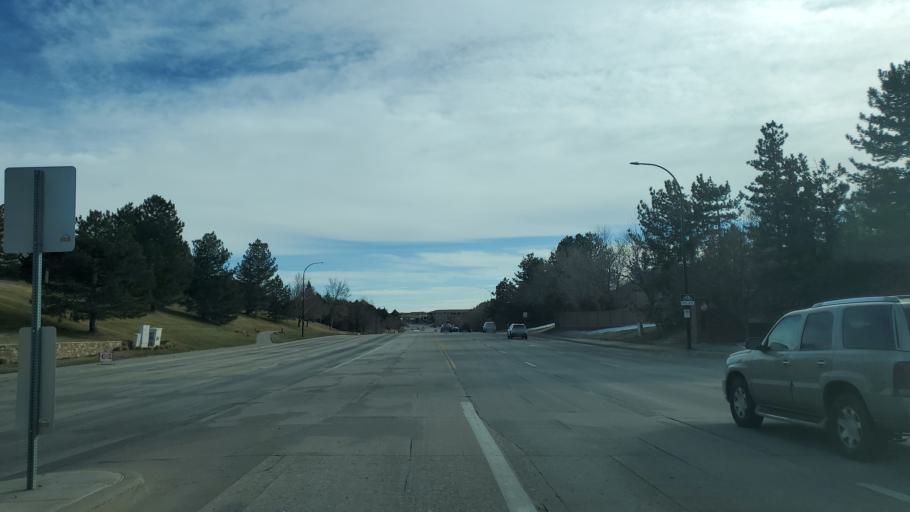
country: US
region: Colorado
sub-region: Douglas County
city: Highlands Ranch
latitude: 39.5577
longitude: -104.9580
